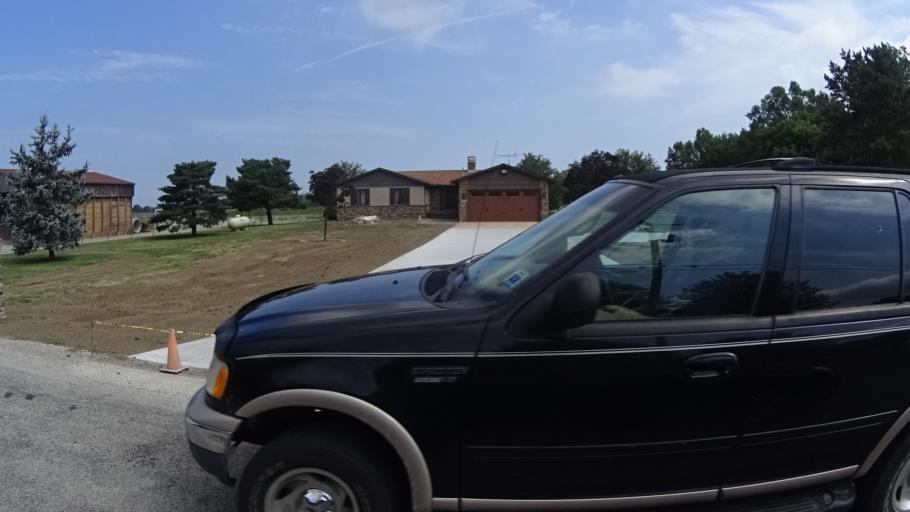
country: US
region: Ohio
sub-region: Lorain County
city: Vermilion
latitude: 41.3833
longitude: -82.4149
